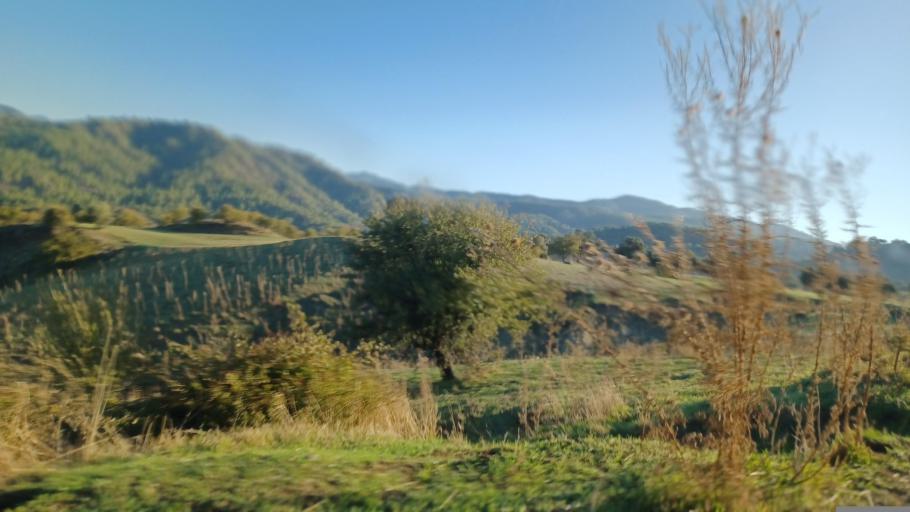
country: CY
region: Pafos
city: Polis
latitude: 34.9510
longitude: 32.5507
